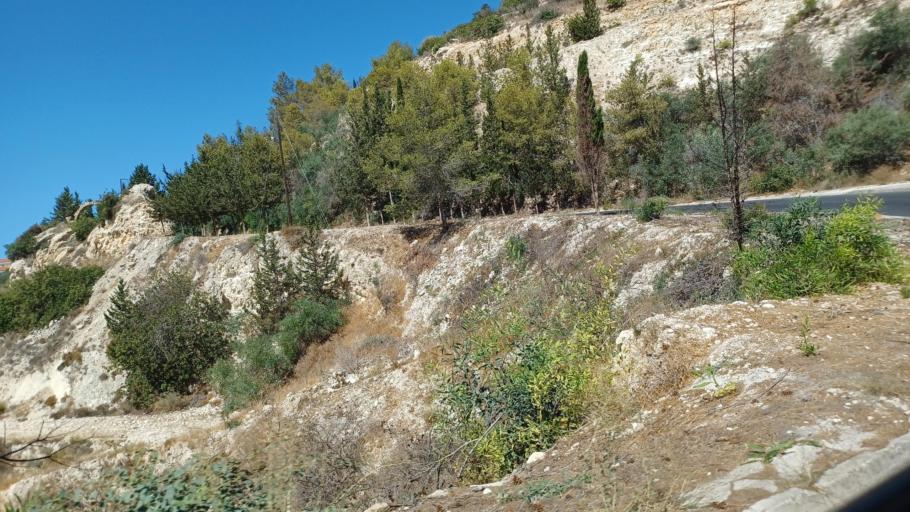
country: CY
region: Pafos
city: Tala
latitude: 34.8492
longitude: 32.4300
